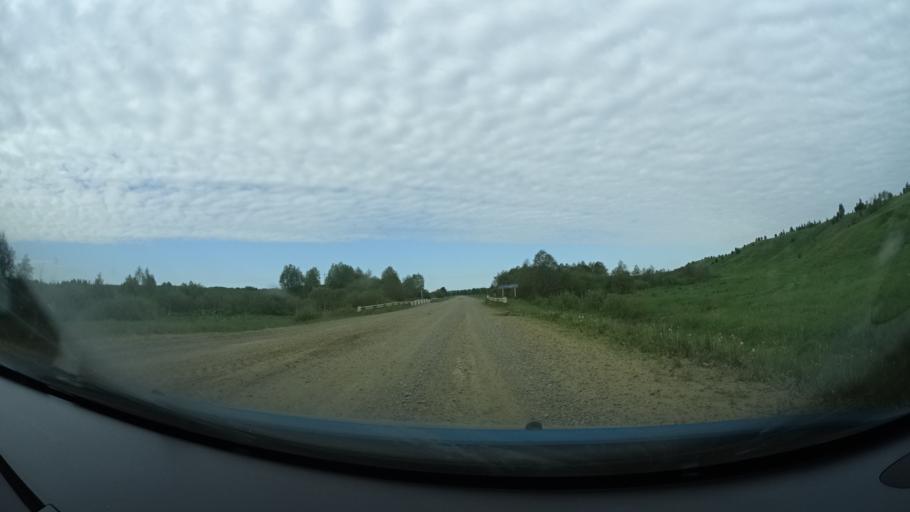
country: RU
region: Perm
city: Kuyeda
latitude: 56.5297
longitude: 55.6402
